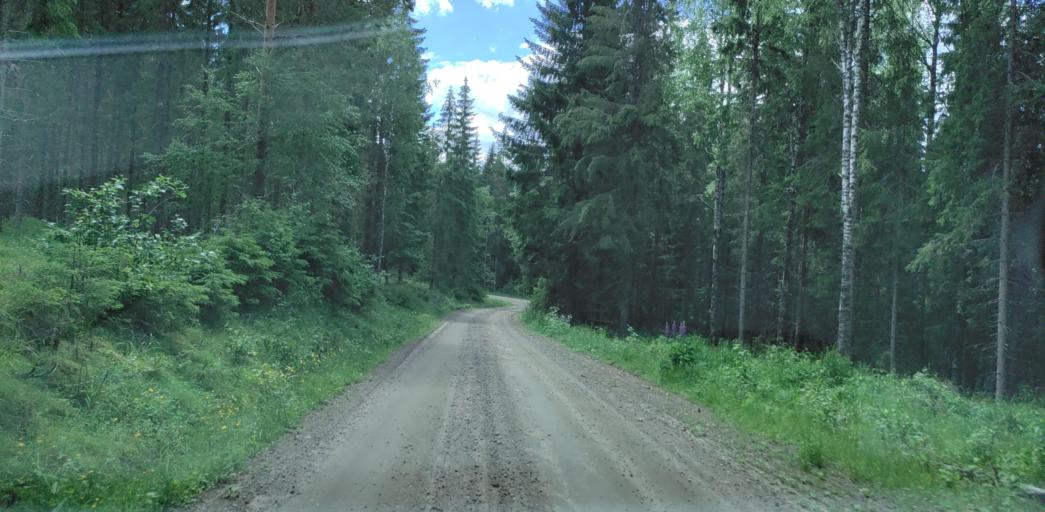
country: SE
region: Vaermland
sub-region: Hagfors Kommun
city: Ekshaerad
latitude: 60.0630
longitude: 13.3064
